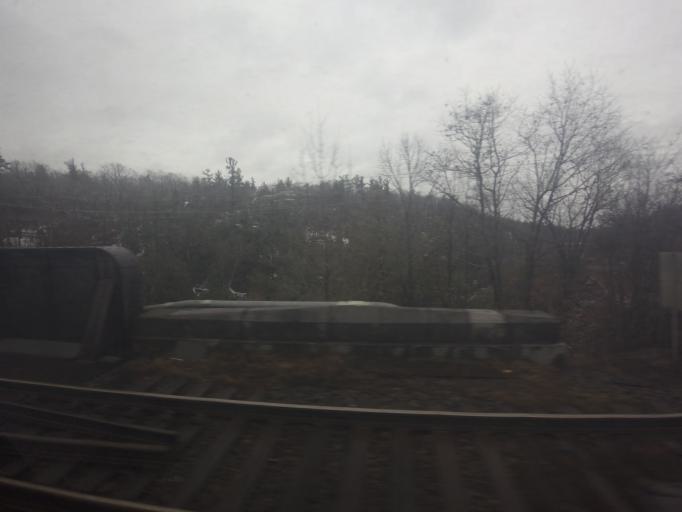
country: CA
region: Ontario
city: Kingston
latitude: 44.2918
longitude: -76.4428
